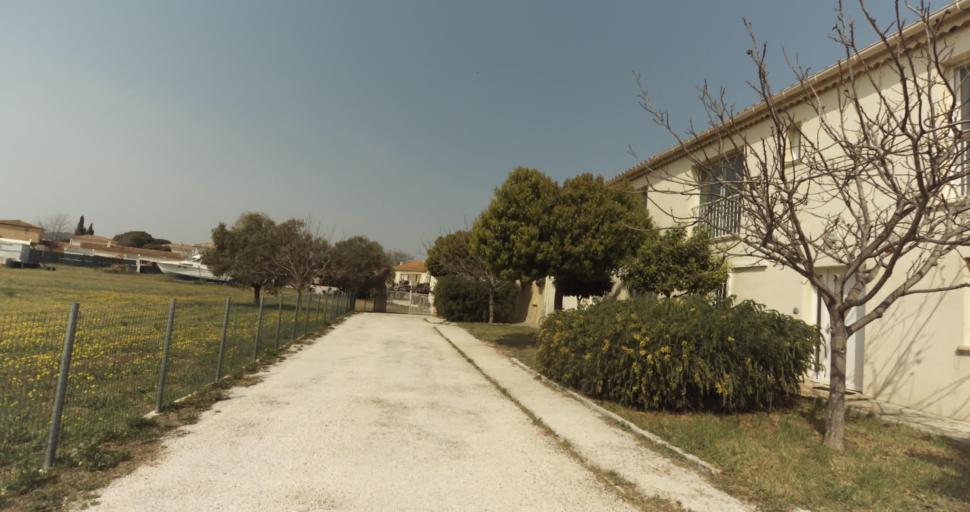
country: FR
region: Provence-Alpes-Cote d'Azur
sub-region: Departement du Var
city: Bormes-les-Mimosas
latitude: 43.1356
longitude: 6.3487
